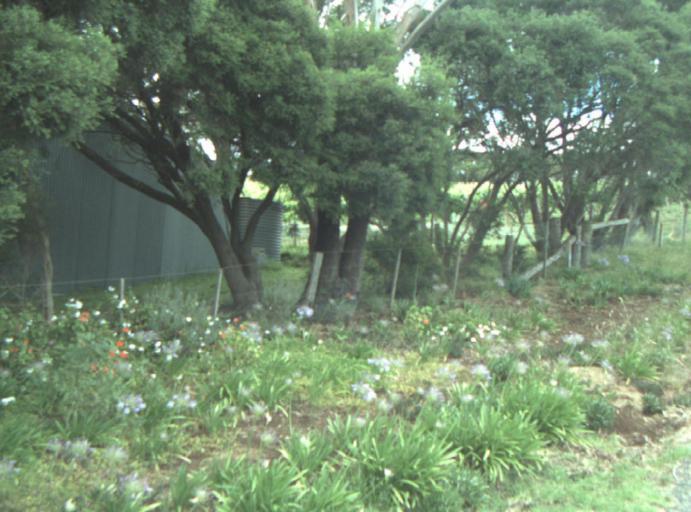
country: AU
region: Victoria
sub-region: Greater Geelong
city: Wandana Heights
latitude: -38.2082
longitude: 144.2841
